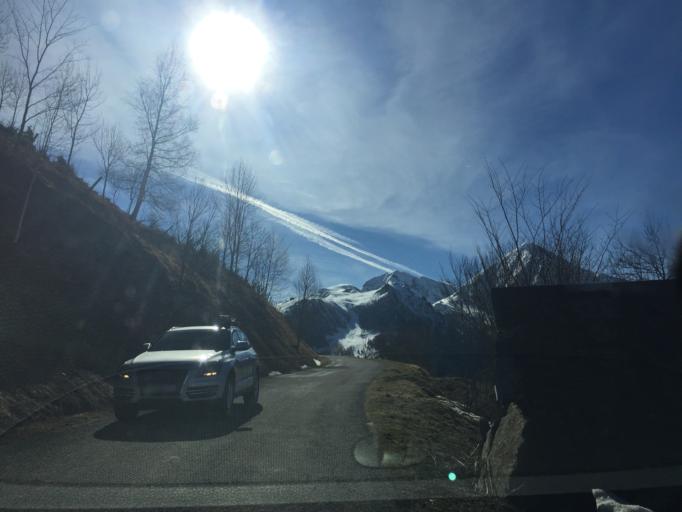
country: FR
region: Midi-Pyrenees
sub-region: Departement des Hautes-Pyrenees
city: Saint-Lary-Soulan
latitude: 42.8077
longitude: 0.3634
